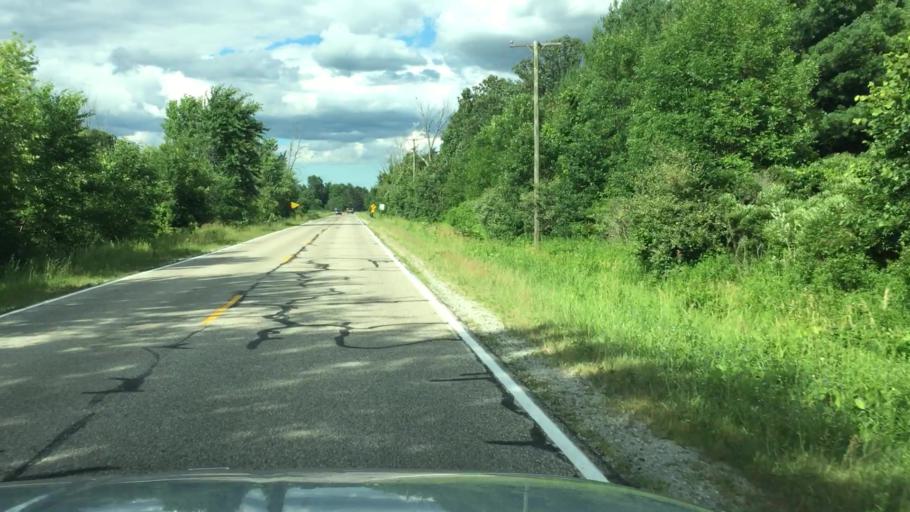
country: US
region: Michigan
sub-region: Saint Clair County
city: Capac
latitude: 43.1090
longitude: -82.9040
